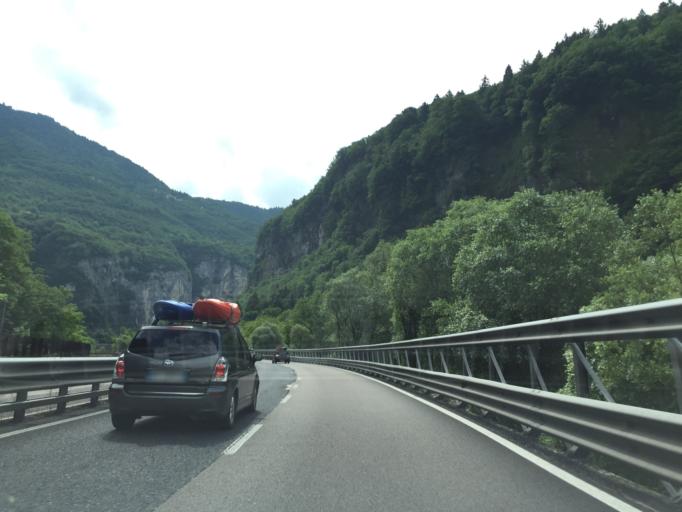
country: IT
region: Veneto
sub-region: Provincia di Vicenza
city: Enego
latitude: 45.9553
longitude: 11.7132
